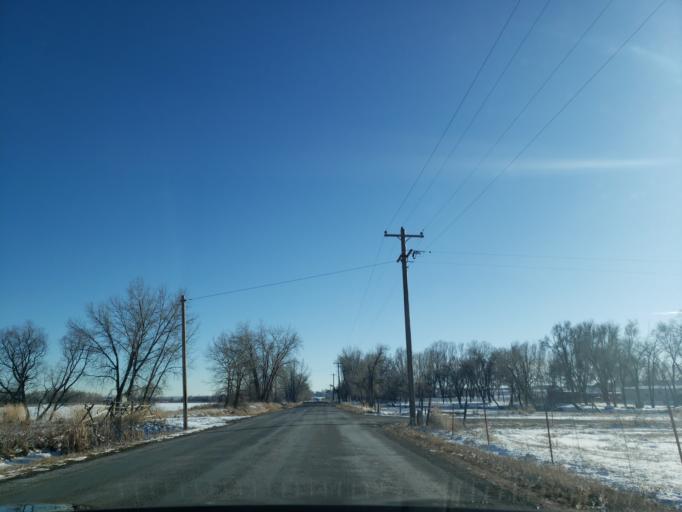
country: US
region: Colorado
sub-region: Larimer County
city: Fort Collins
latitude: 40.5307
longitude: -105.0013
